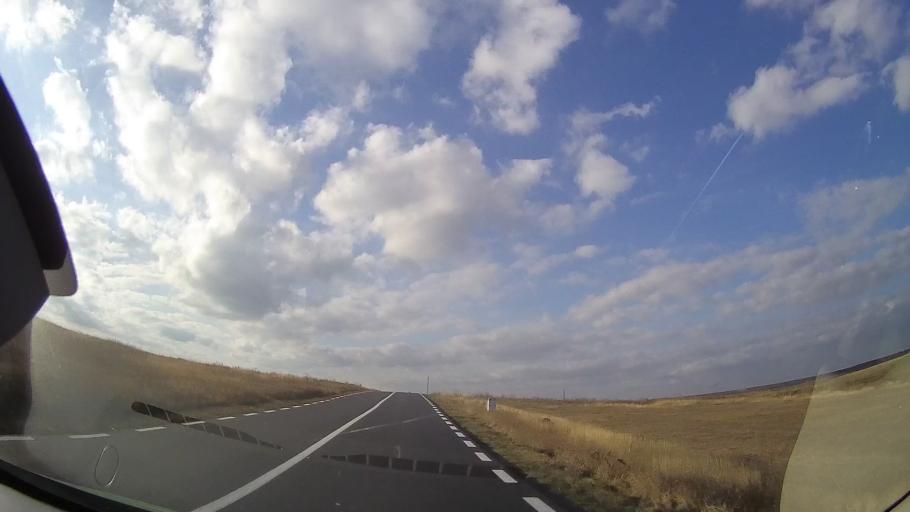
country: RO
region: Constanta
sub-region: Comuna Albesti
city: Albesti
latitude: 43.8089
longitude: 28.4155
